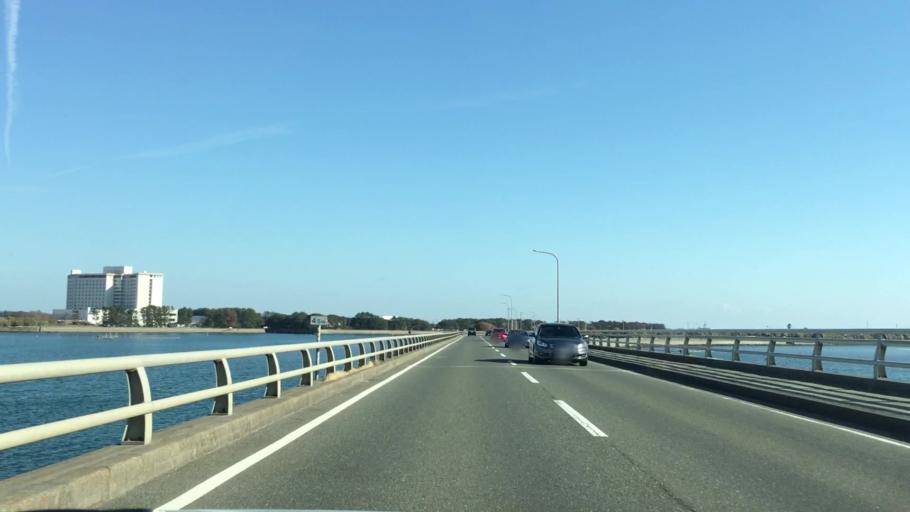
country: JP
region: Shizuoka
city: Kosai-shi
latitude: 34.7103
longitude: 137.6070
